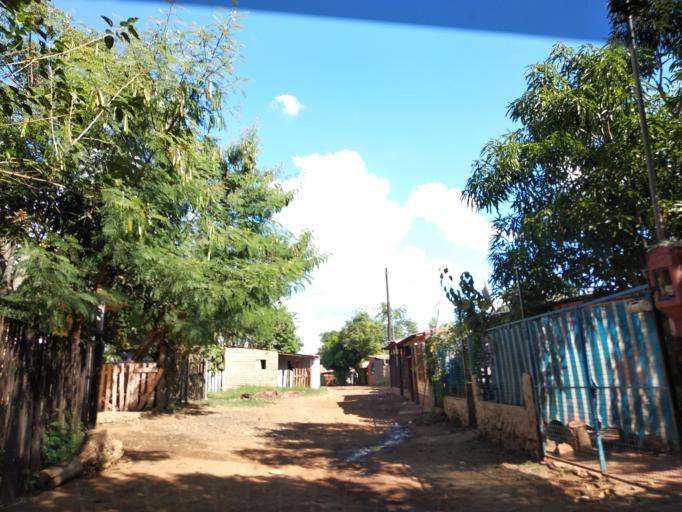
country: AR
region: Misiones
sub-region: Departamento de Capital
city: Posadas
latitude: -27.3904
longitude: -55.9465
